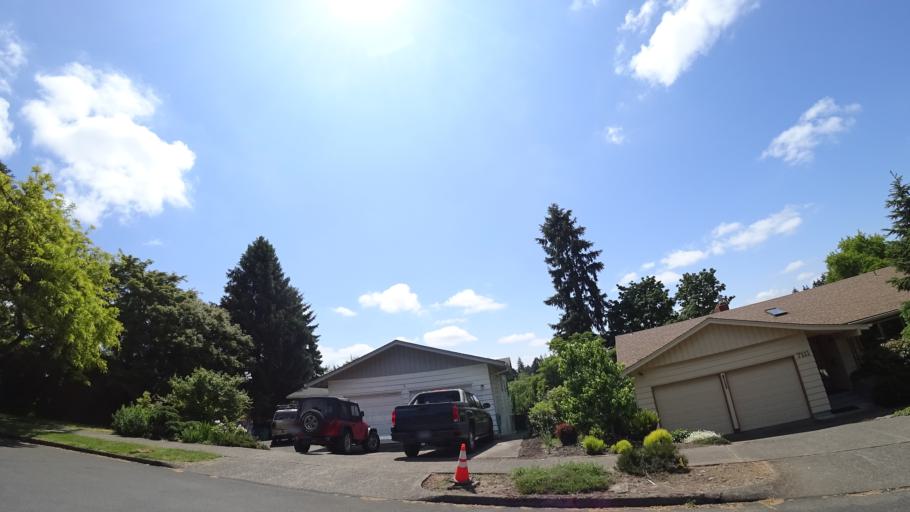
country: US
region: Oregon
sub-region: Multnomah County
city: Portland
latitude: 45.4729
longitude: -122.6927
